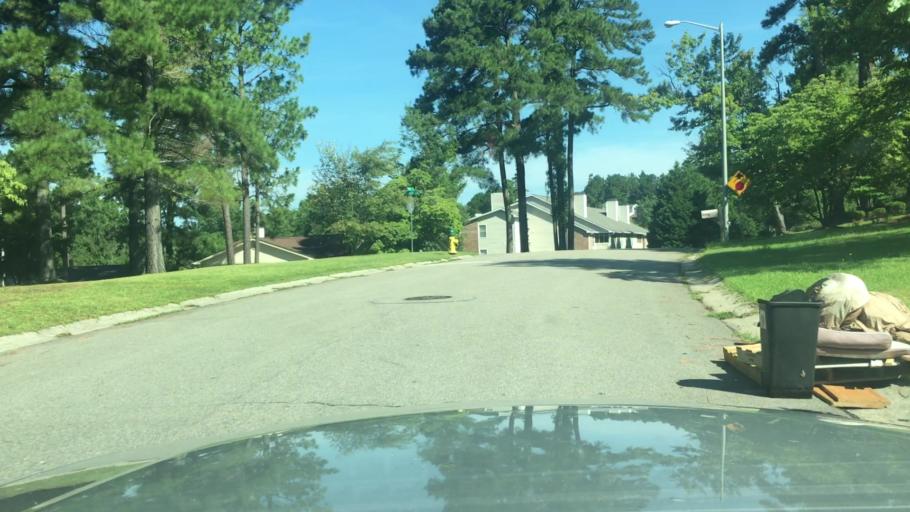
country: US
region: North Carolina
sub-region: Cumberland County
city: Fayetteville
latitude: 35.1077
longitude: -78.9104
